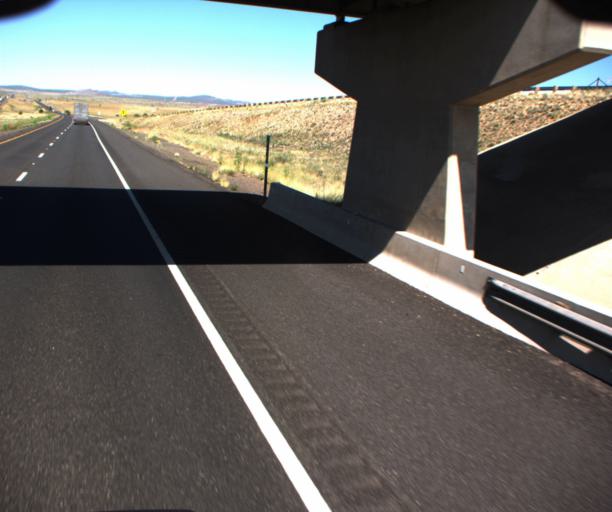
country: US
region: Arizona
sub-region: Yavapai County
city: Paulden
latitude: 35.2297
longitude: -112.5856
